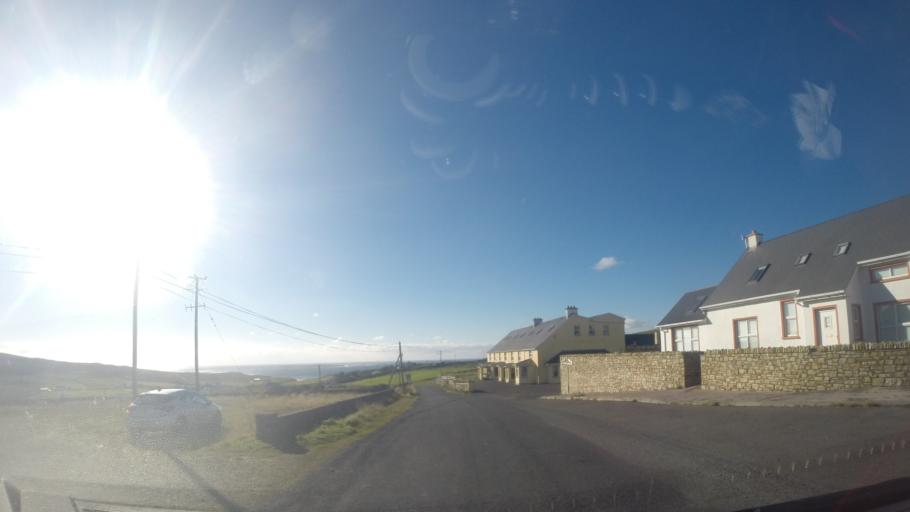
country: IE
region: Ulster
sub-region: County Donegal
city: Killybegs
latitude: 54.6966
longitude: -8.7700
